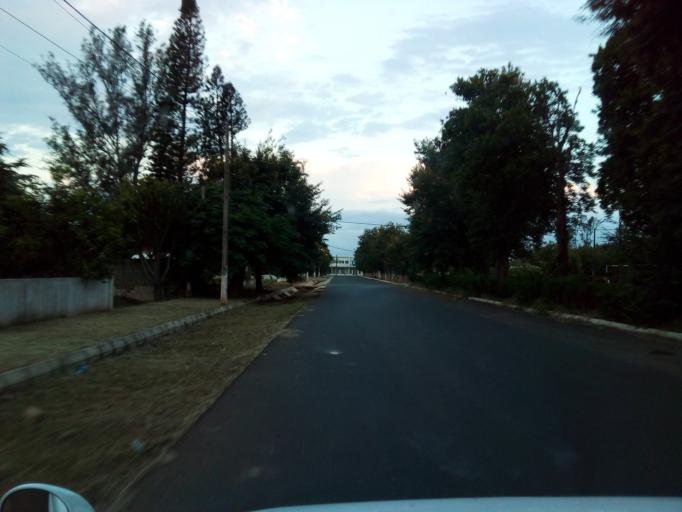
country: MZ
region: Maputo City
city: Maputo
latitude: -26.3445
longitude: 32.6765
